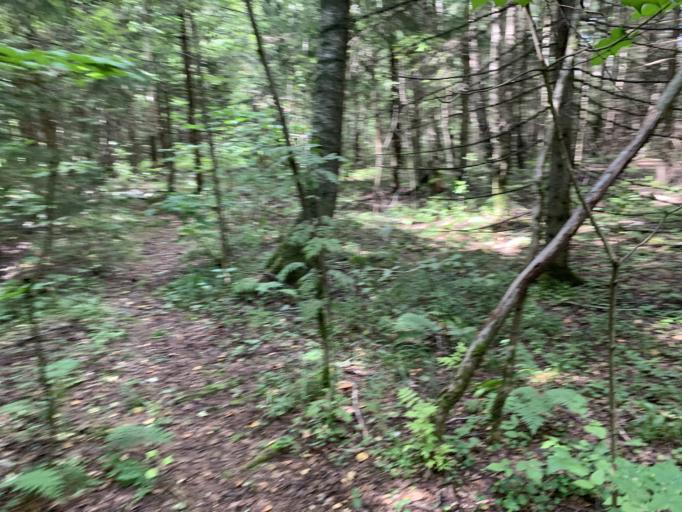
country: RU
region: Moskovskaya
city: Podosinki
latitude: 56.1778
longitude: 37.5697
